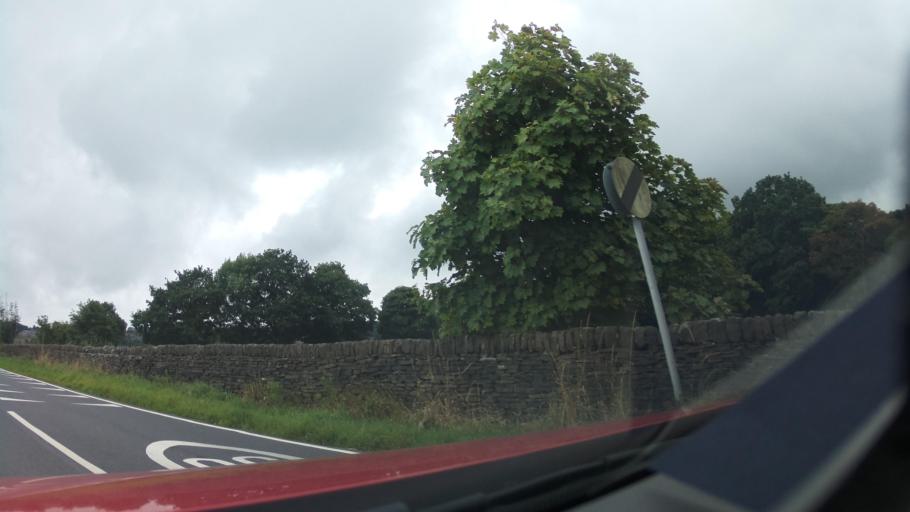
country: GB
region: England
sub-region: Kirklees
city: Shelley
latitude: 53.5845
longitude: -1.6882
